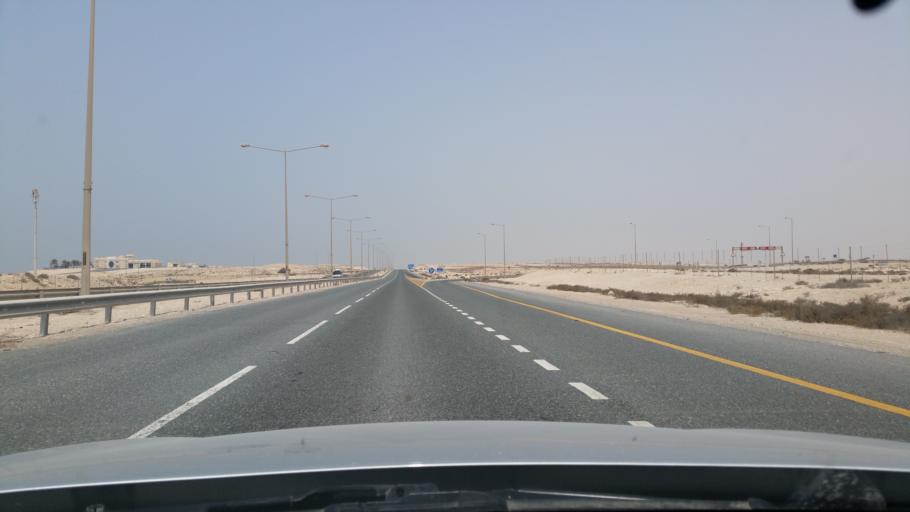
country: QA
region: Baladiyat ar Rayyan
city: Dukhan
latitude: 25.3219
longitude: 50.7887
